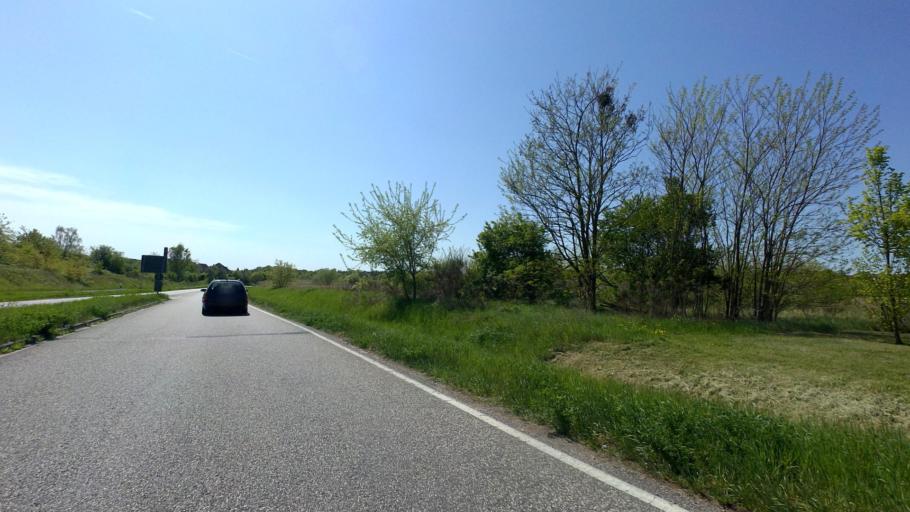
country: DE
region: Brandenburg
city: Konigs Wusterhausen
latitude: 52.3018
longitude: 13.6022
